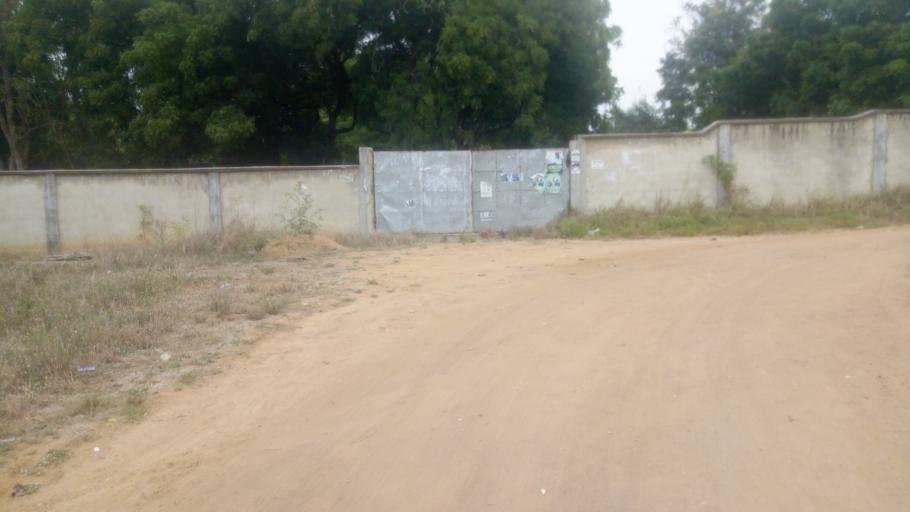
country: GH
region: Central
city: Winneba
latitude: 5.3613
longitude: -0.6296
